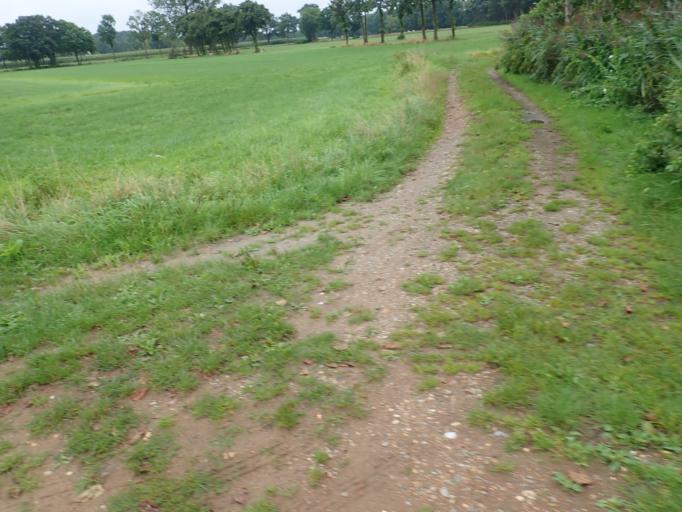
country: BE
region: Flanders
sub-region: Provincie Antwerpen
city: Zoersel
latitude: 51.2501
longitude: 4.7131
